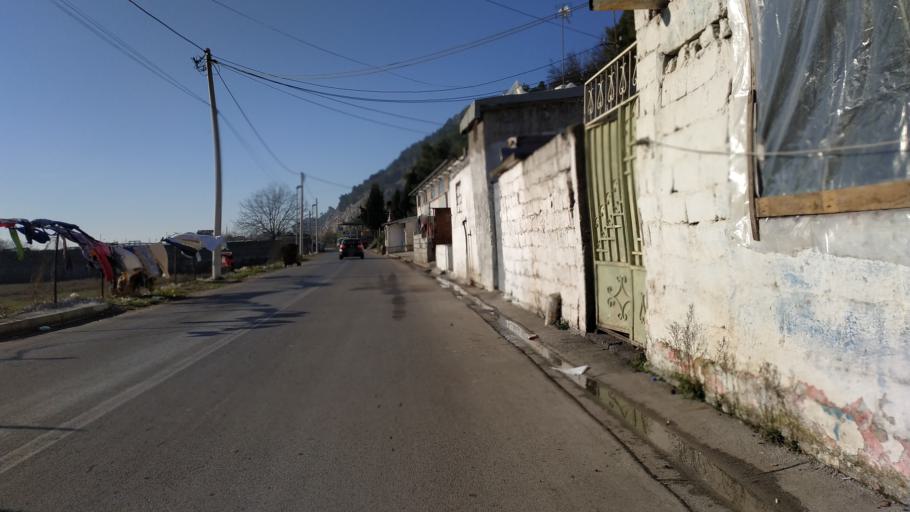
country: AL
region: Shkoder
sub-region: Rrethi i Shkodres
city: Shkoder
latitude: 42.0504
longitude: 19.4889
